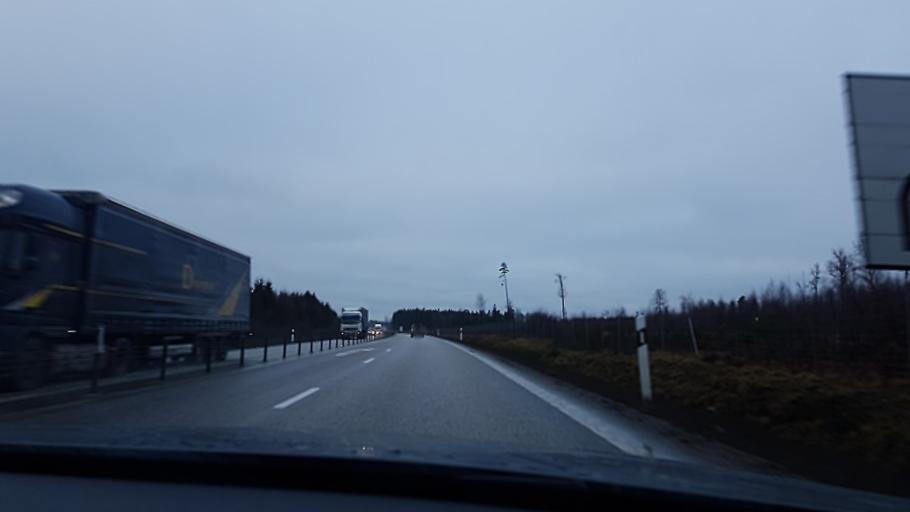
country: SE
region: Kronoberg
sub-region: Ljungby Kommun
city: Lagan
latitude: 56.9954
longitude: 14.0271
